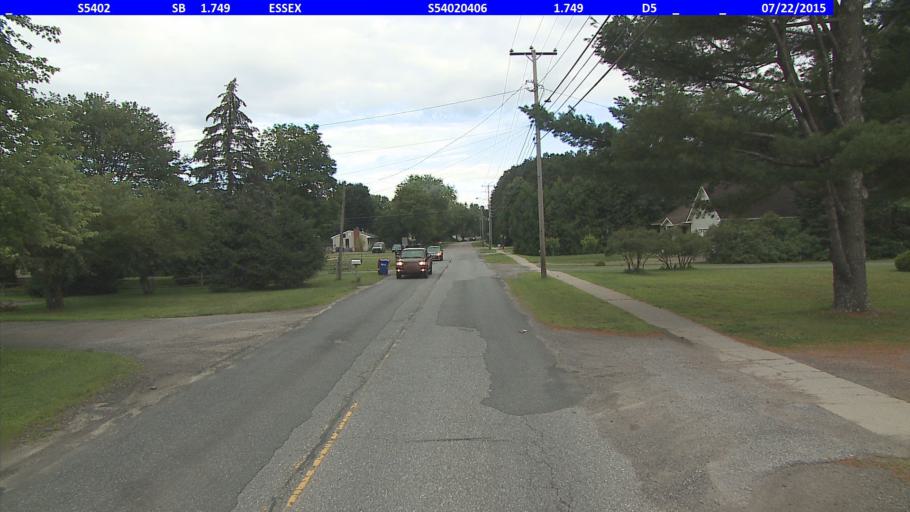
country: US
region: Vermont
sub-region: Chittenden County
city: Jericho
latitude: 44.5030
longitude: -73.0508
